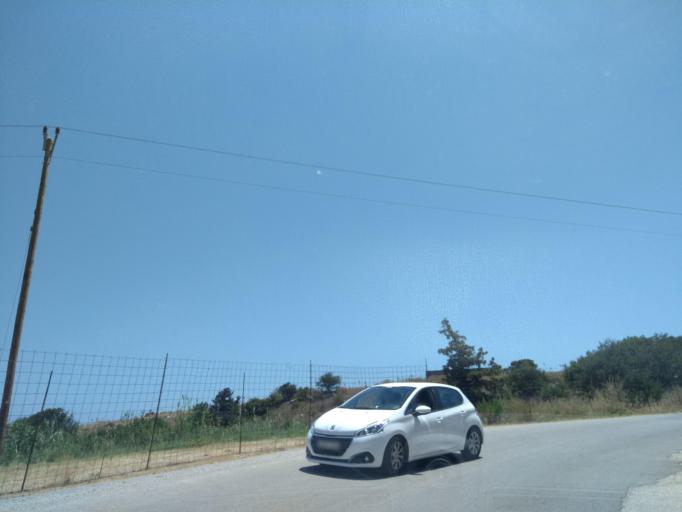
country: GR
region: Crete
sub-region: Nomos Chanias
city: Georgioupolis
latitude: 35.3196
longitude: 24.2892
